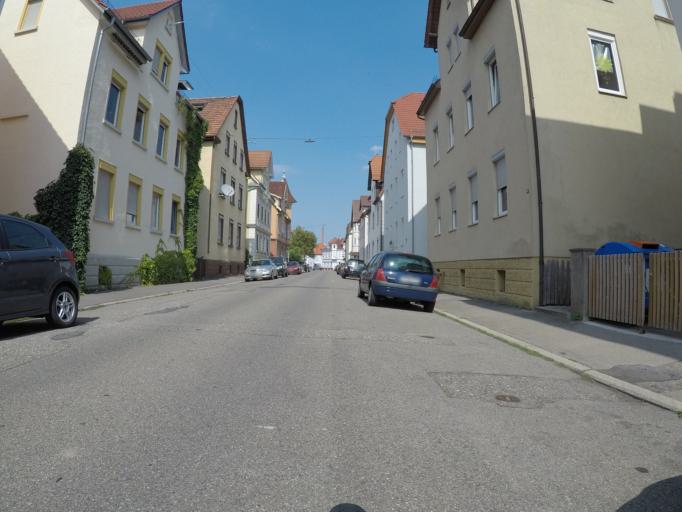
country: DE
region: Baden-Wuerttemberg
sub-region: Tuebingen Region
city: Reutlingen
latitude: 48.4939
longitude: 9.2000
